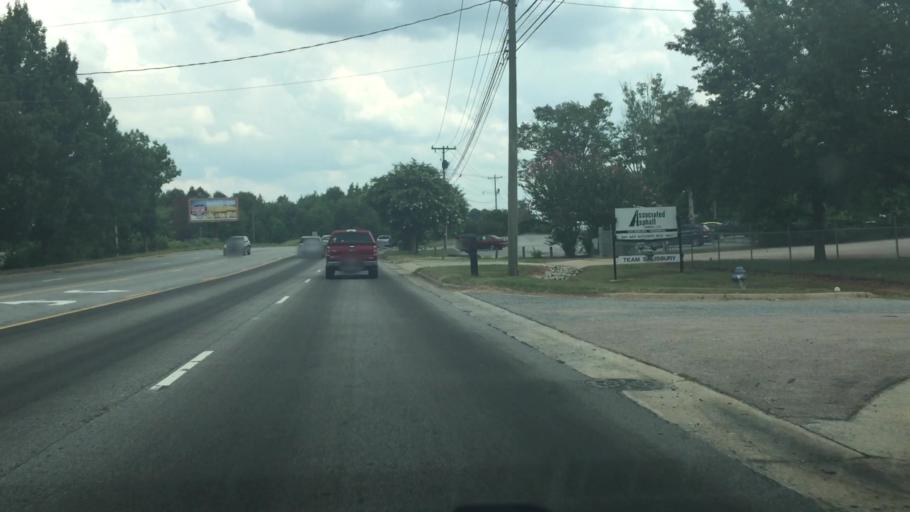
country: US
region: North Carolina
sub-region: Rowan County
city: Franklin
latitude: 35.6868
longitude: -80.5092
